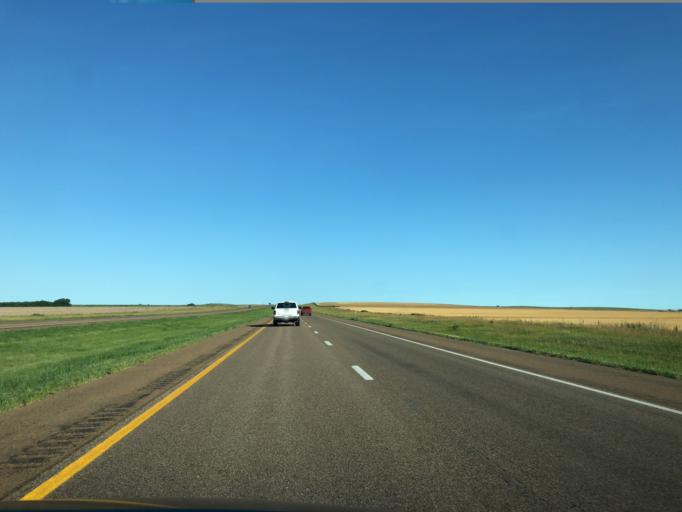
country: US
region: Kansas
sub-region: Ellis County
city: Ellis
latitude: 38.9736
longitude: -99.6727
